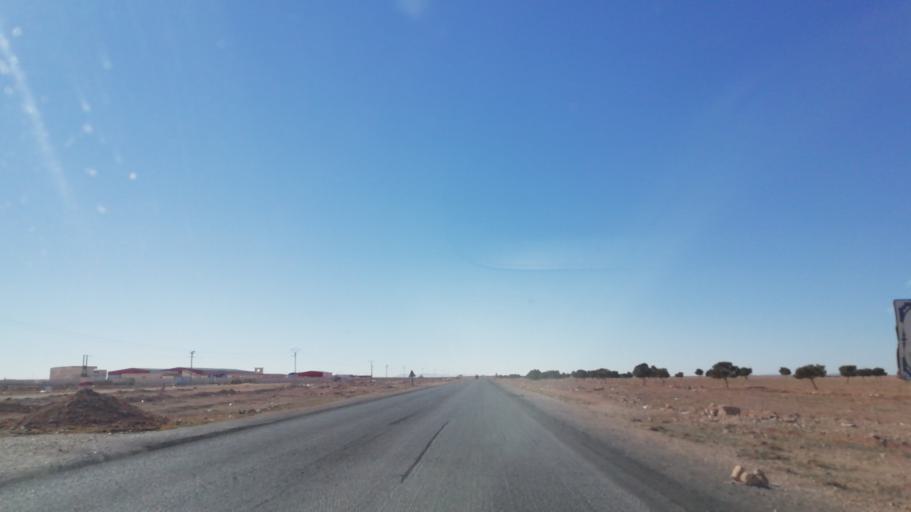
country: DZ
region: Saida
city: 'Ain el Hadjar
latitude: 34.0250
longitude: 0.0686
